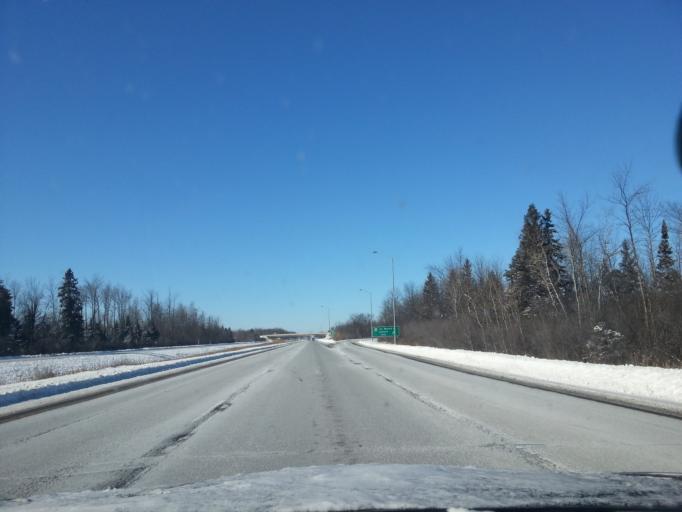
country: CA
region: Ontario
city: Carleton Place
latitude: 45.3115
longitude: -76.0478
